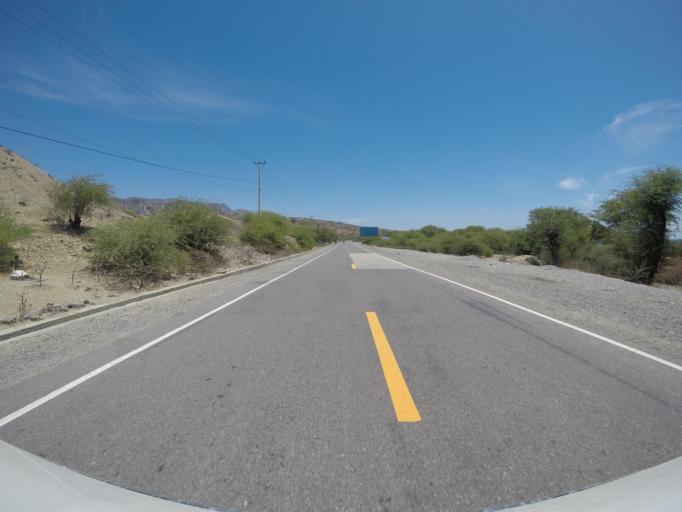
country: TL
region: Manatuto
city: Manatuto
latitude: -8.4996
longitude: 125.9974
